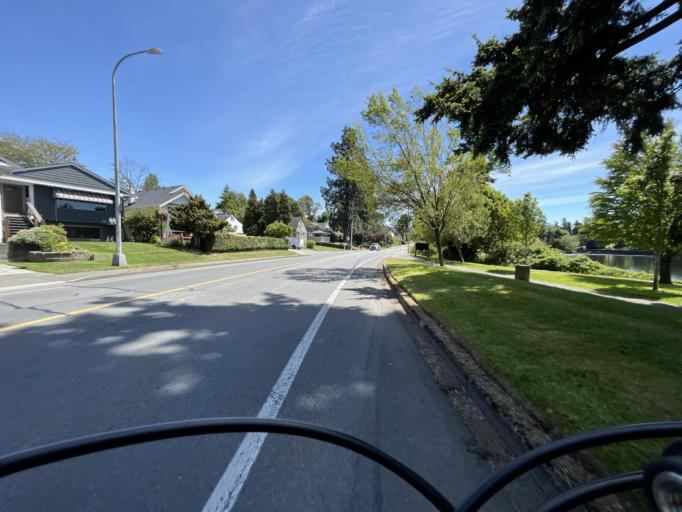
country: CA
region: British Columbia
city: Victoria
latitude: 48.4491
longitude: -123.4053
